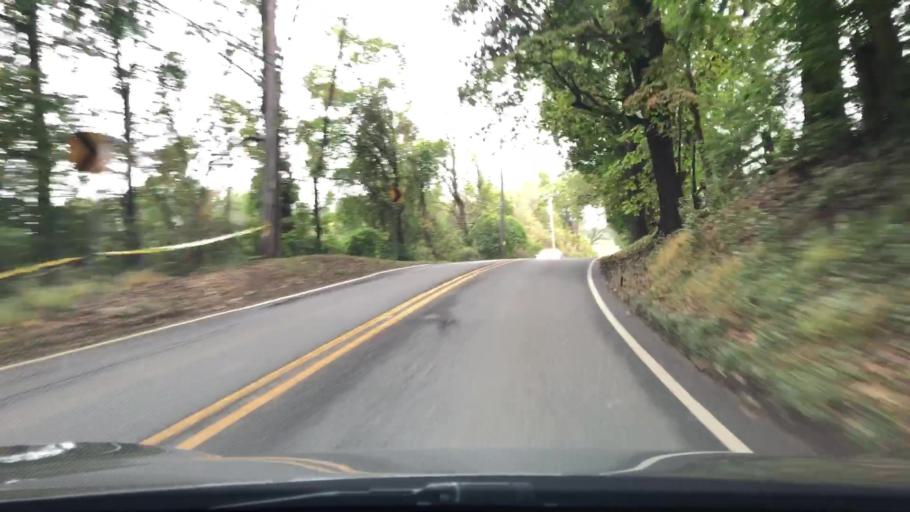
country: US
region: Pennsylvania
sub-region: Delaware County
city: Wayne
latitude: 40.0166
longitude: -75.3891
